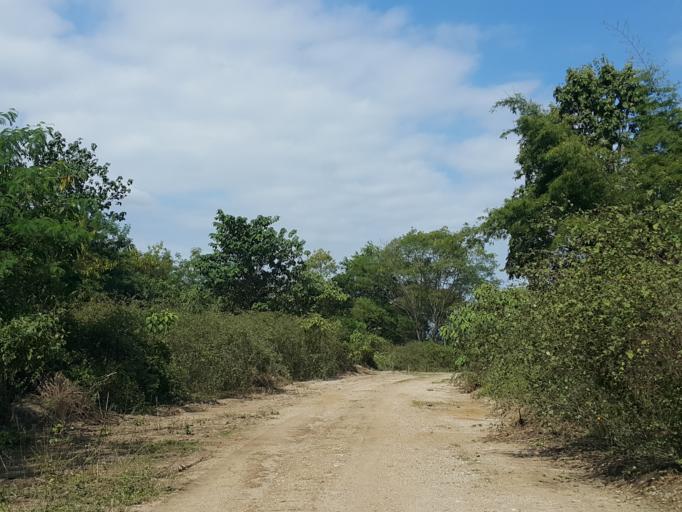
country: TH
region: Lampang
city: Mae Mo
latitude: 18.3312
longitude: 99.7658
